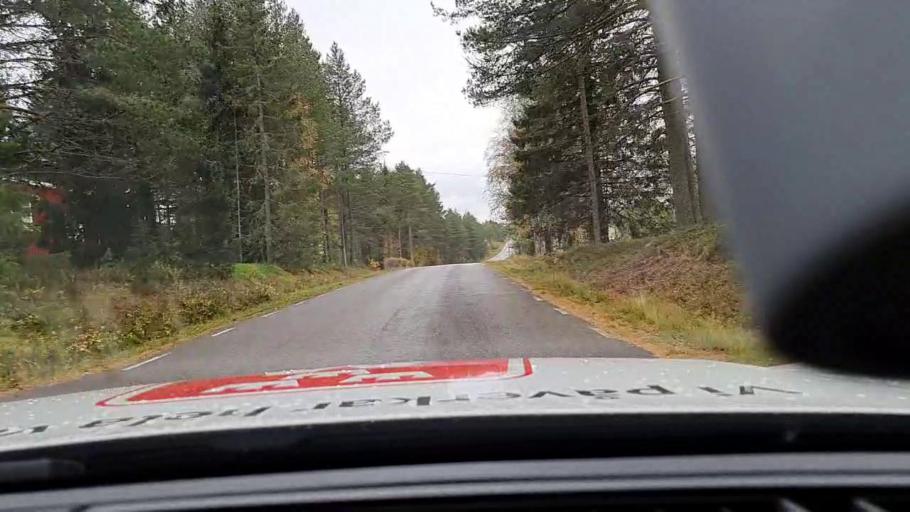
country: SE
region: Norrbotten
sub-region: Haparanda Kommun
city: Haparanda
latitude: 65.7852
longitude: 23.9207
